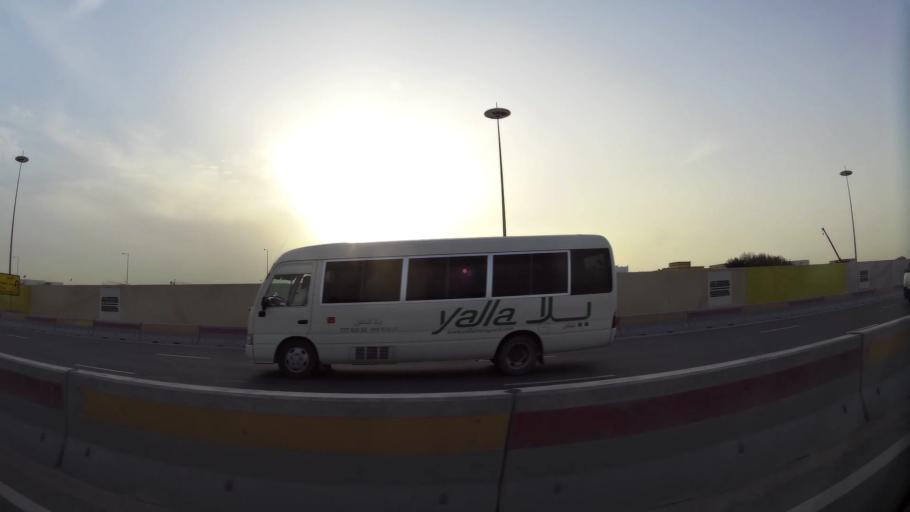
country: QA
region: Baladiyat ad Dawhah
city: Doha
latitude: 25.3472
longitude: 51.5210
